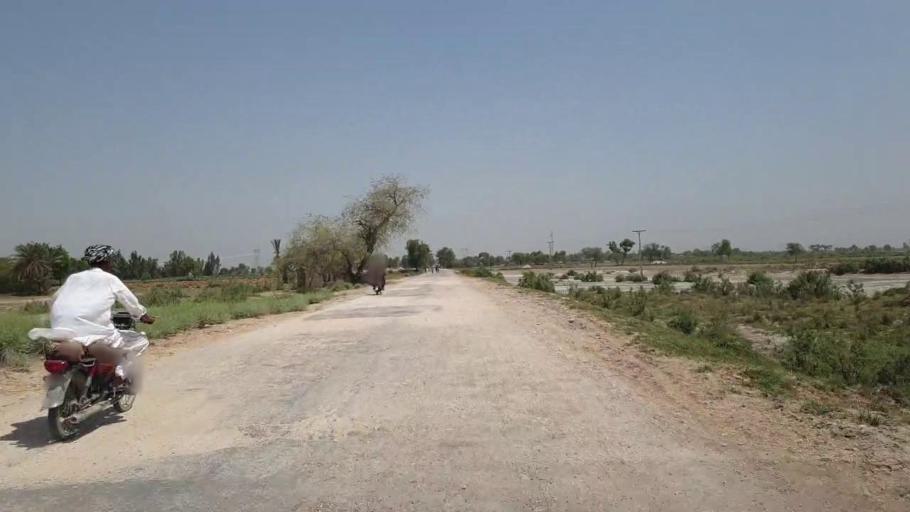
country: PK
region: Sindh
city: Adilpur
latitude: 27.8837
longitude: 69.2876
